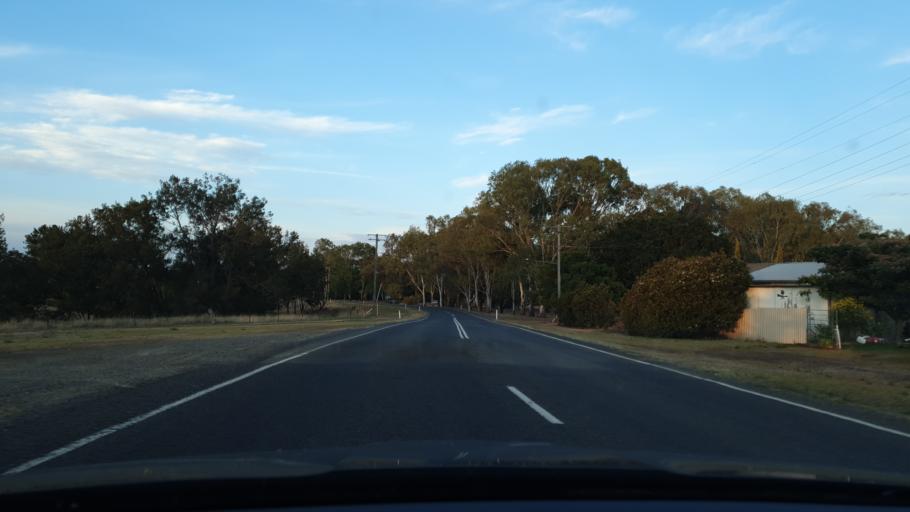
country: AU
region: Queensland
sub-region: Southern Downs
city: Warwick
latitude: -28.0308
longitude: 151.9815
